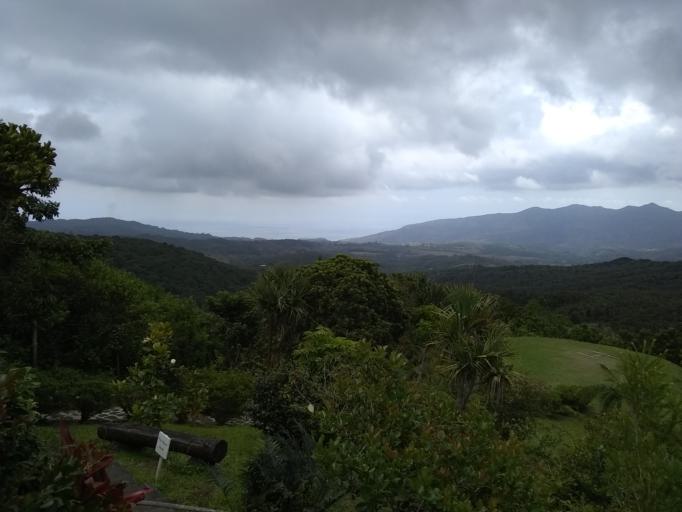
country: MU
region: Black River
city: Petite Case Noyale
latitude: -20.4260
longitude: 57.4175
